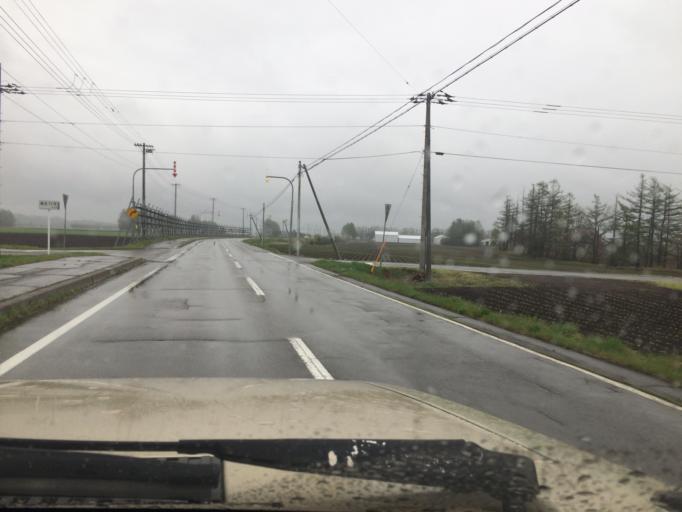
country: JP
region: Hokkaido
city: Obihiro
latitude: 42.8432
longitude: 142.9981
